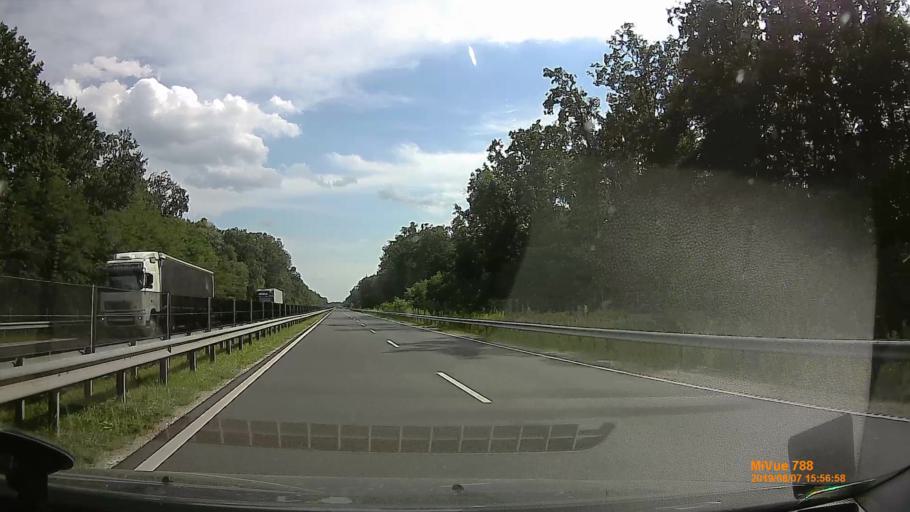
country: HU
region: Vas
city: Kormend
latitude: 47.0512
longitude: 16.6149
